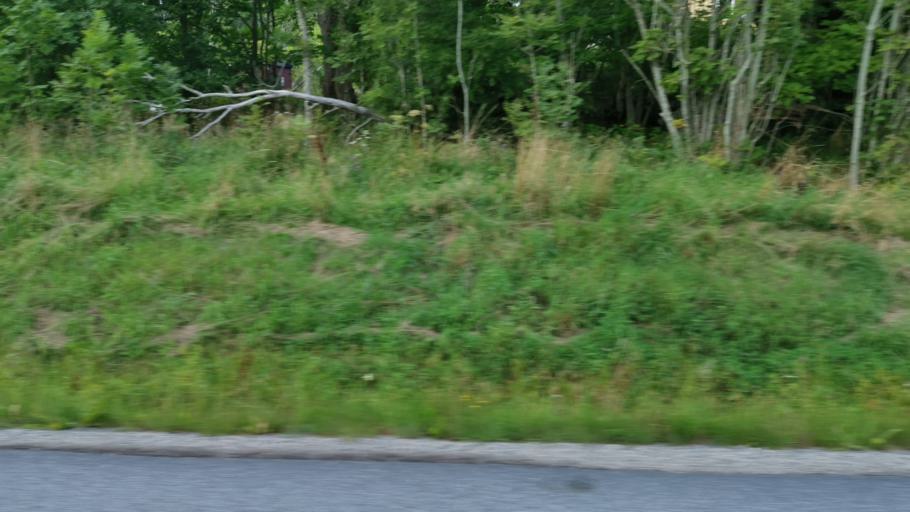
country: SE
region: Vaestra Goetaland
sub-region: Sotenas Kommun
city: Hunnebostrand
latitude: 58.4736
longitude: 11.4054
